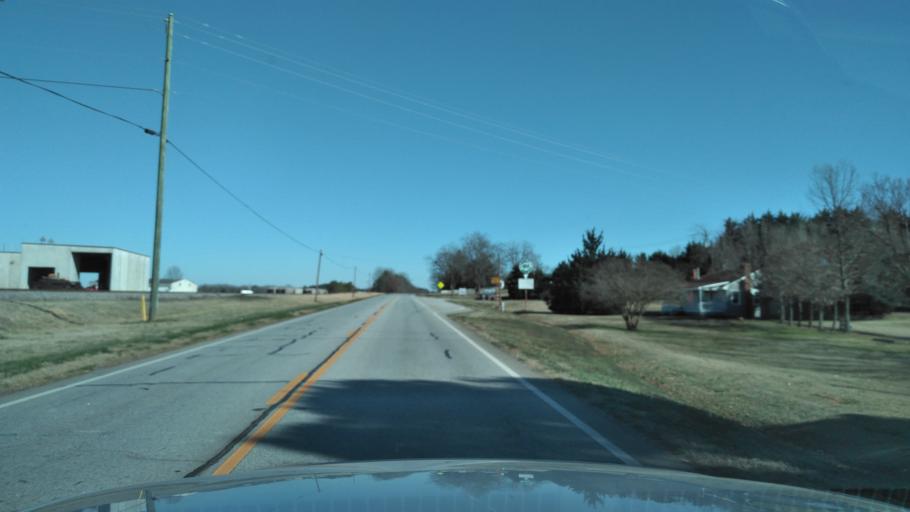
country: US
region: Georgia
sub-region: Banks County
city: Maysville
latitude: 34.2443
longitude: -83.5463
